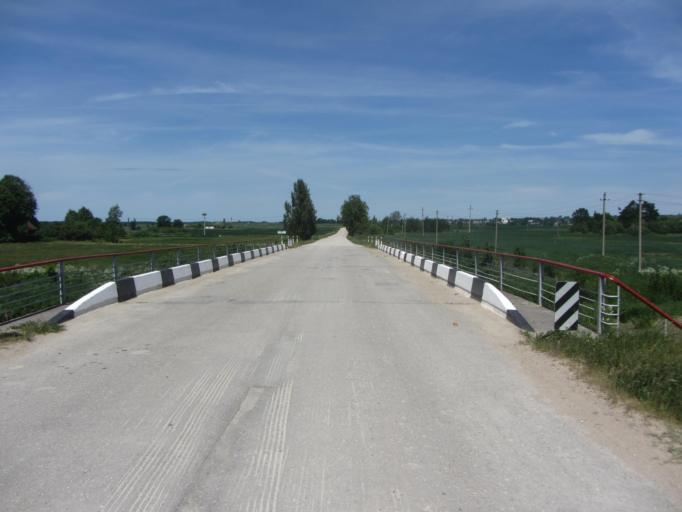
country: LT
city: Jieznas
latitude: 54.5716
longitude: 24.3177
